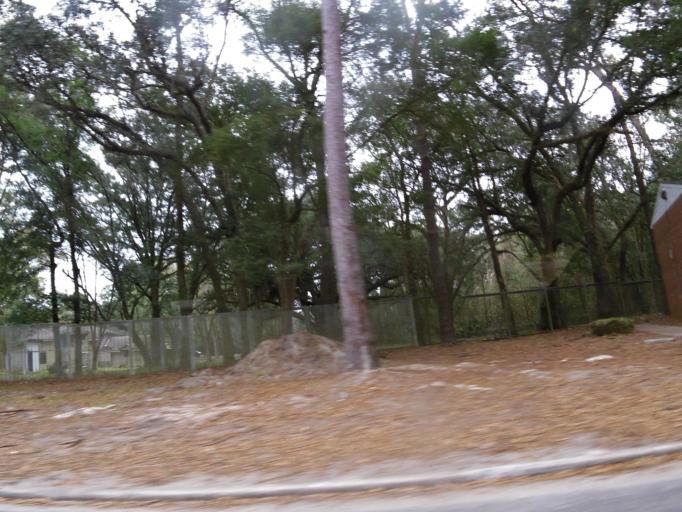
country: US
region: Florida
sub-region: Duval County
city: Jacksonville
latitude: 30.3897
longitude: -81.7140
